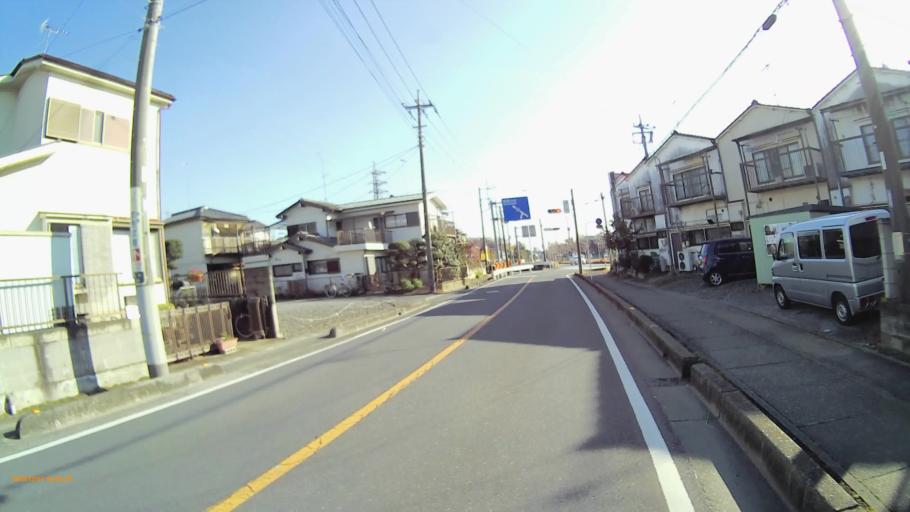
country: JP
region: Saitama
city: Fukiage-fujimi
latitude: 36.0950
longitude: 139.4631
